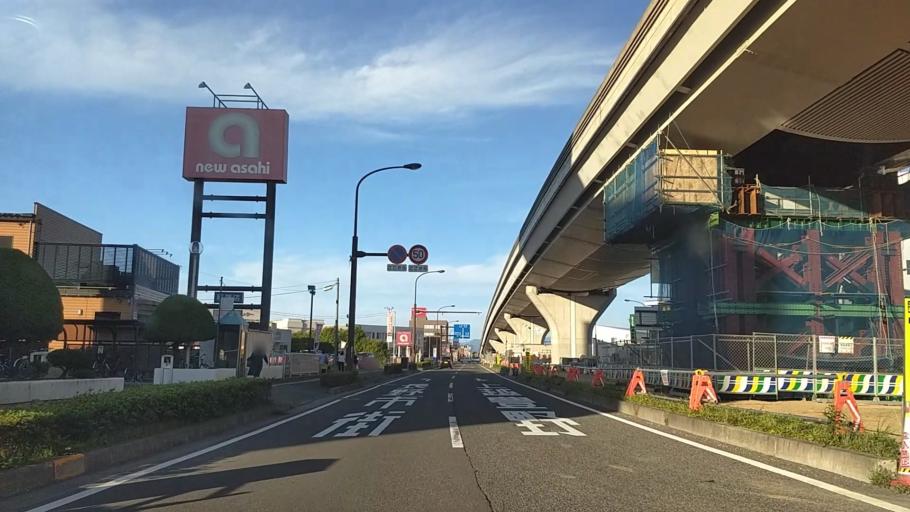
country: JP
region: Nagano
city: Nagano-shi
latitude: 36.6291
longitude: 138.2017
